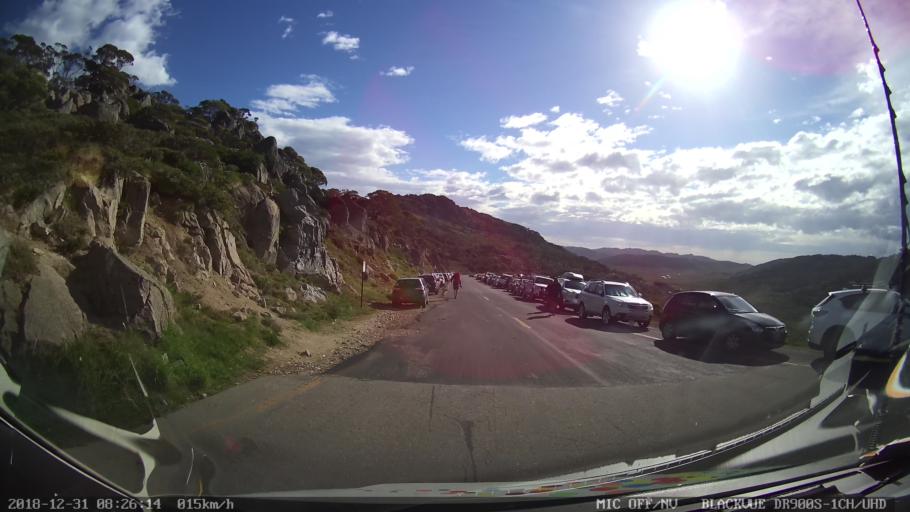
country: AU
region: New South Wales
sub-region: Snowy River
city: Jindabyne
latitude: -36.4315
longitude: 148.3293
